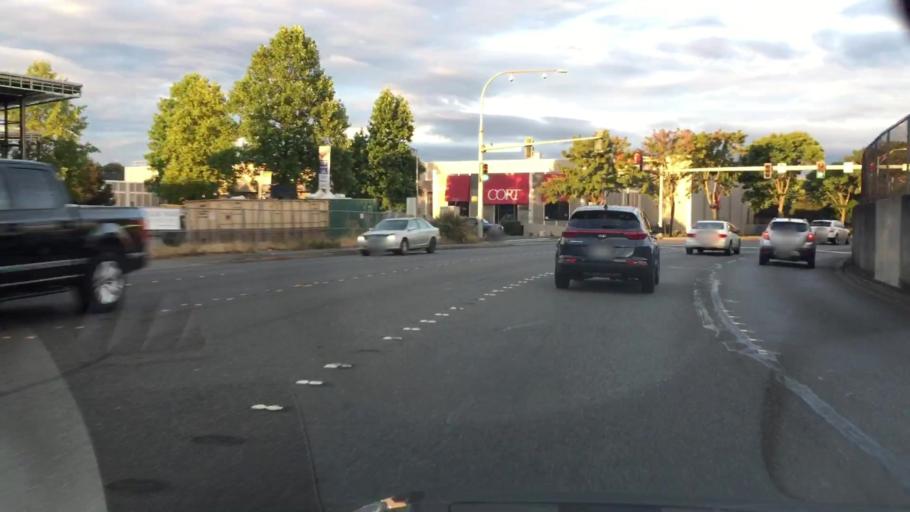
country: US
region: Washington
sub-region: King County
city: Tukwila
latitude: 47.4417
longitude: -122.2519
